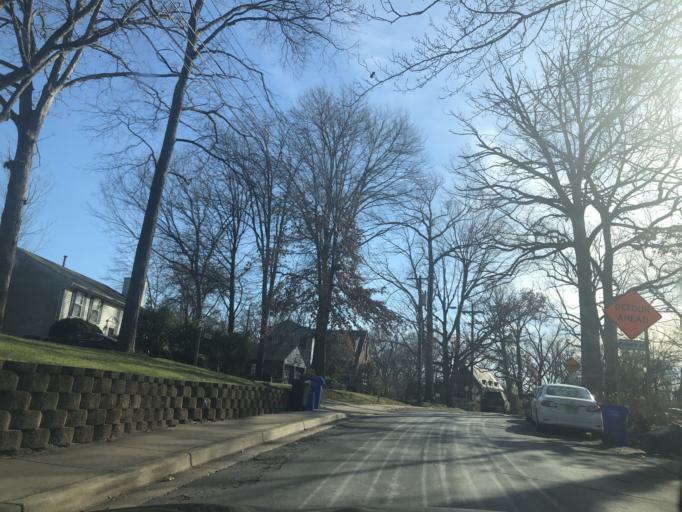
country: US
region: Maryland
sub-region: Montgomery County
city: Four Corners
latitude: 39.0023
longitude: -77.0061
